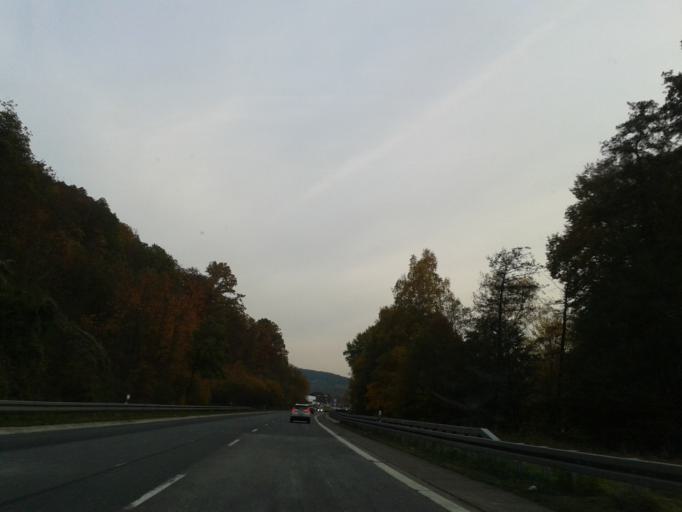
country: DE
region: Hesse
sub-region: Regierungsbezirk Giessen
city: Sinn
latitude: 50.6619
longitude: 8.3253
